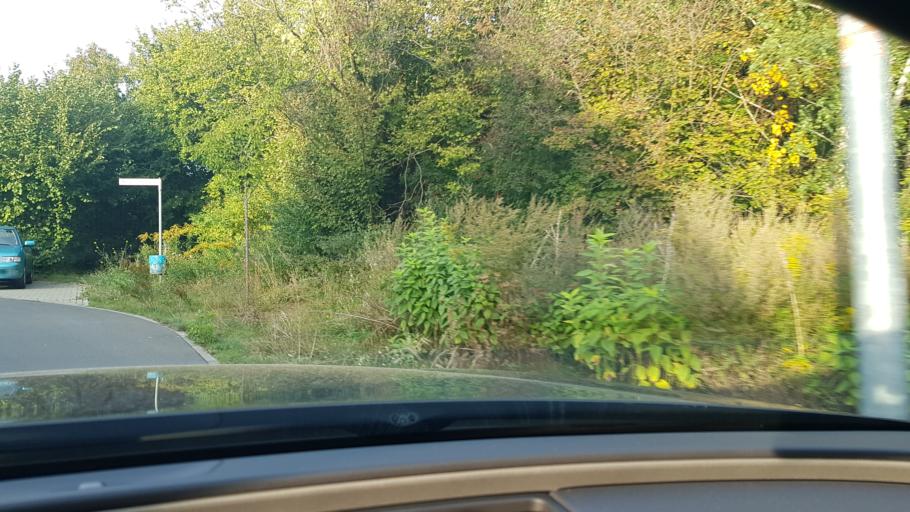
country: DE
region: Brandenburg
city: Brieselang
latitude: 52.5954
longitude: 12.9900
